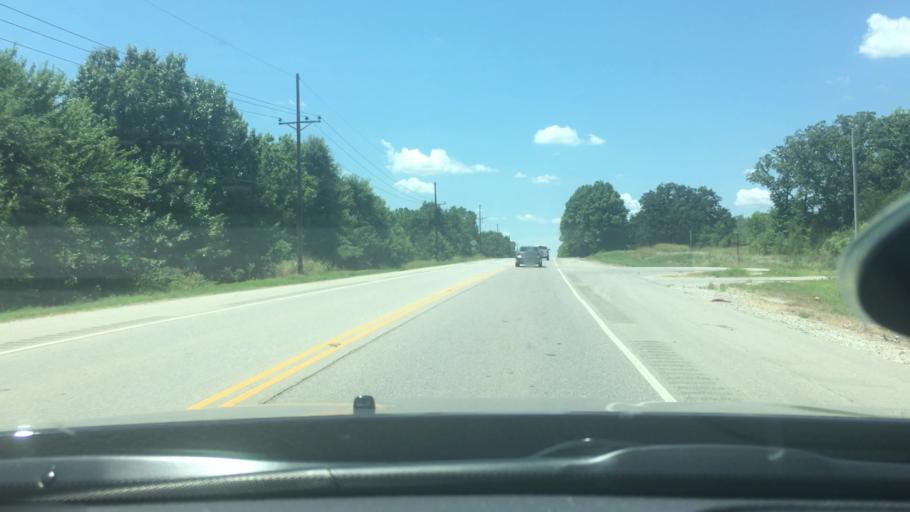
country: US
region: Oklahoma
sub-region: Bryan County
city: Durant
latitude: 34.0041
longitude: -96.1981
